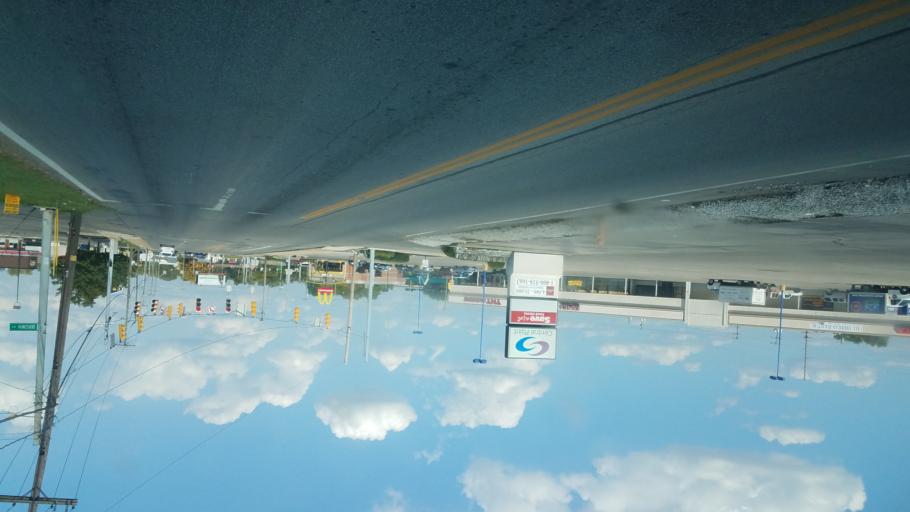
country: US
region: Ohio
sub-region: Franklin County
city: Grandview Heights
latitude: 39.9434
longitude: -83.0375
